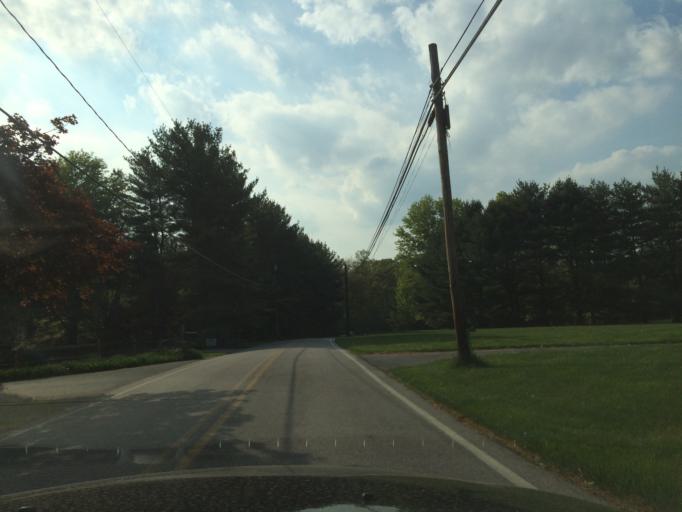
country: US
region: Maryland
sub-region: Howard County
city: Highland
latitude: 39.2195
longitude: -76.9995
